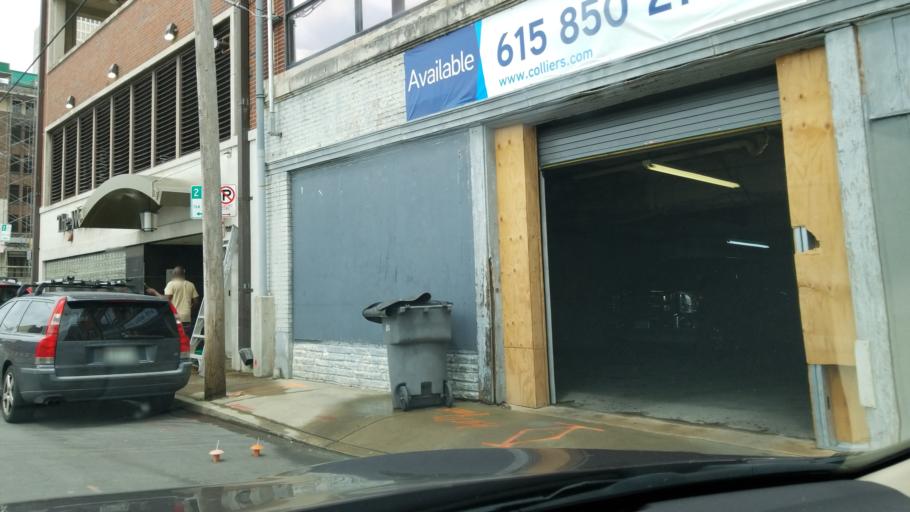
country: US
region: Tennessee
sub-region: Davidson County
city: Nashville
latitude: 36.1607
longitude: -86.7841
